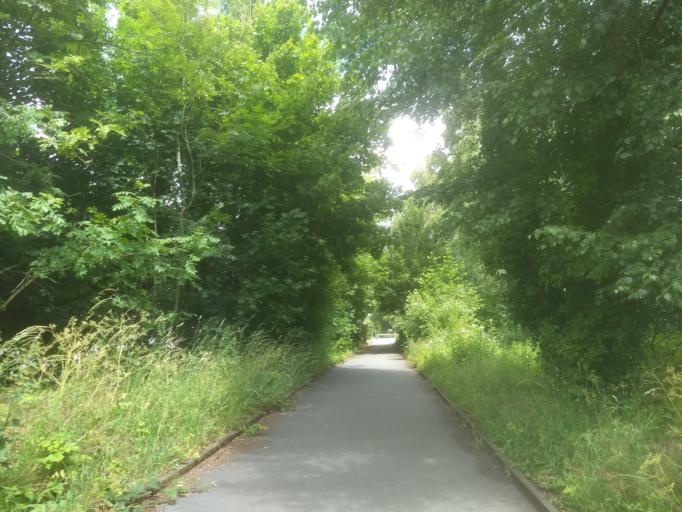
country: FR
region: Nord-Pas-de-Calais
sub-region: Departement du Pas-de-Calais
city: Beaumetz-les-Loges
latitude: 50.2391
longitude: 2.6609
